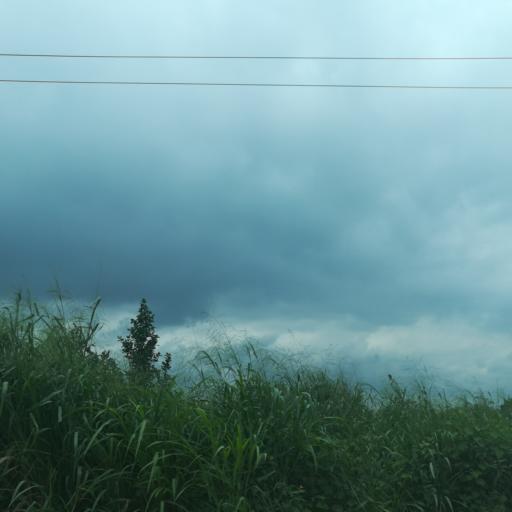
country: NG
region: Lagos
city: Ejirin
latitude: 6.6464
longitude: 3.8406
